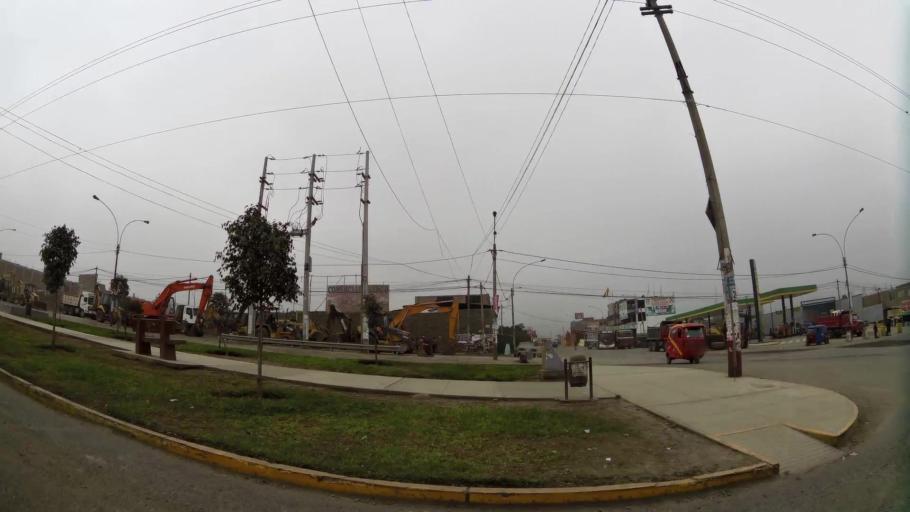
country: PE
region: Lima
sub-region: Lima
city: Urb. Santo Domingo
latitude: -11.9255
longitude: -76.9637
